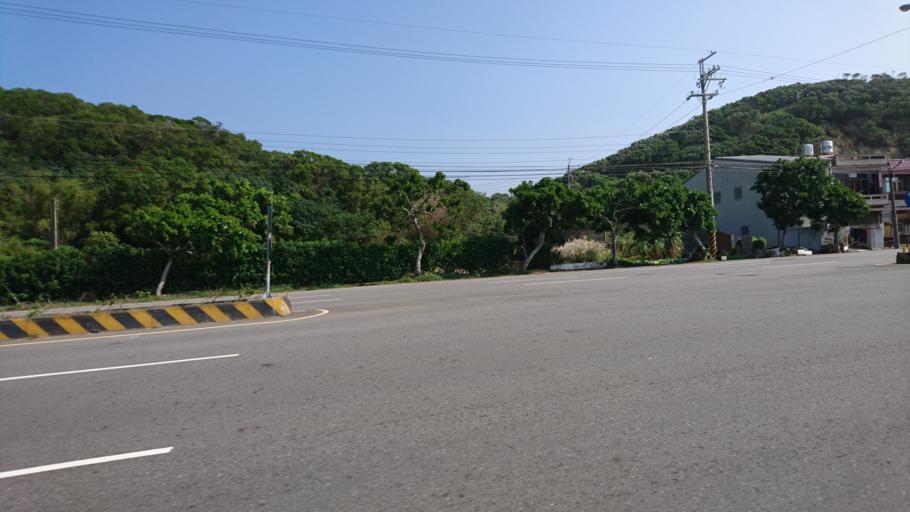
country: TW
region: Taiwan
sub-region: Miaoli
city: Miaoli
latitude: 24.5209
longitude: 120.6920
